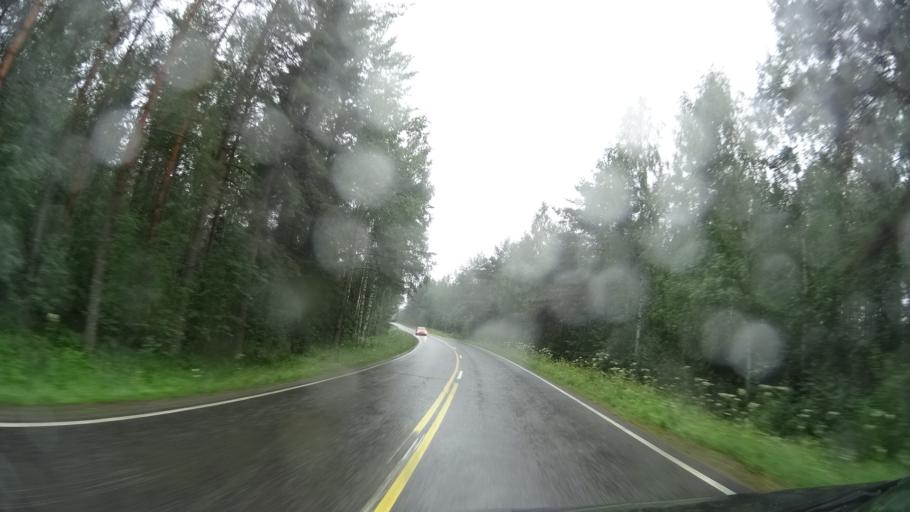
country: FI
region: North Karelia
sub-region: Keski-Karjala
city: Raeaekkylae
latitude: 62.3058
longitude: 29.5540
